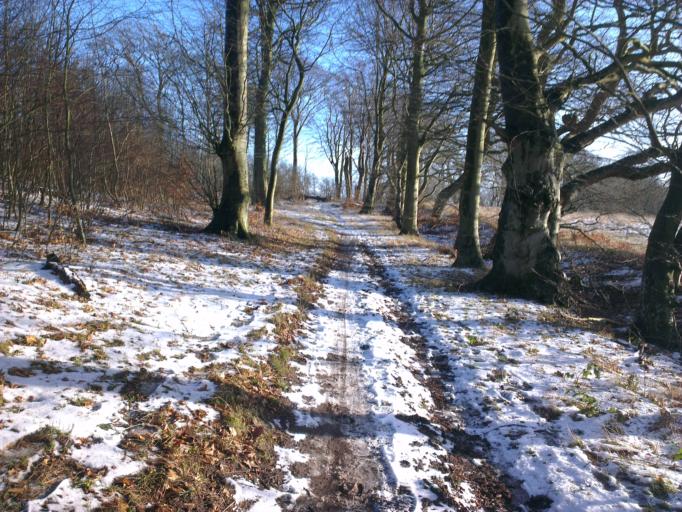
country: DK
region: Capital Region
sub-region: Frederikssund Kommune
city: Frederikssund
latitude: 55.8376
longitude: 12.0281
